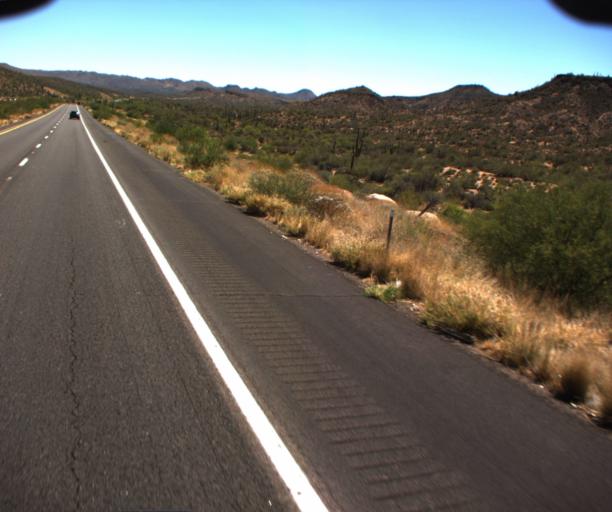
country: US
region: Arizona
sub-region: Maricopa County
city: Rio Verde
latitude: 33.7803
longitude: -111.4932
